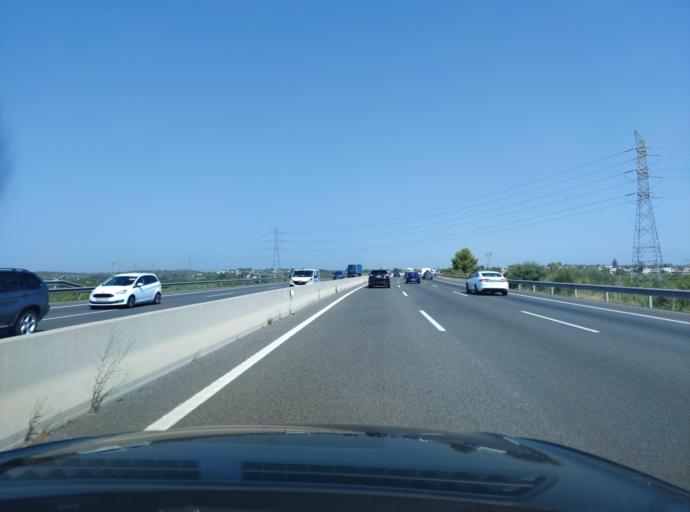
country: ES
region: Valencia
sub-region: Provincia de Valencia
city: Picassent
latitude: 39.3779
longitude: -0.4654
